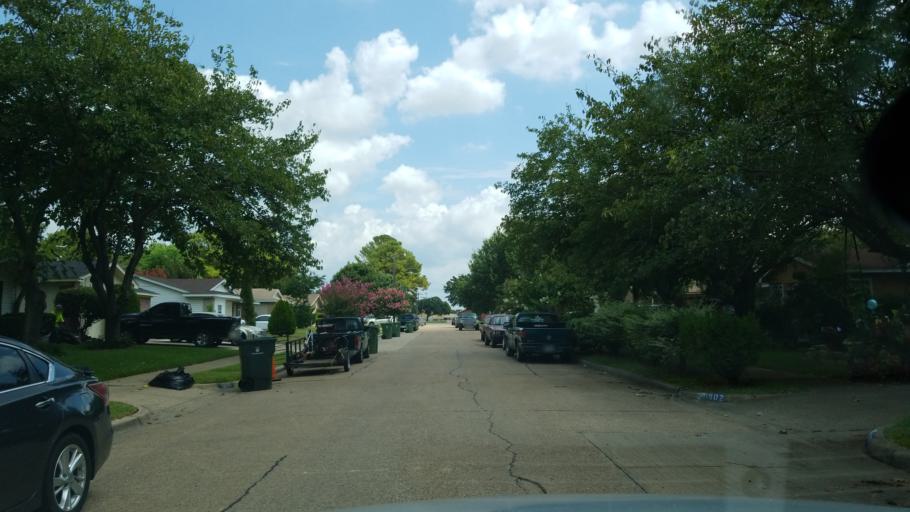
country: US
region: Texas
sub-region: Dallas County
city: Garland
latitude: 32.9226
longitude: -96.6503
